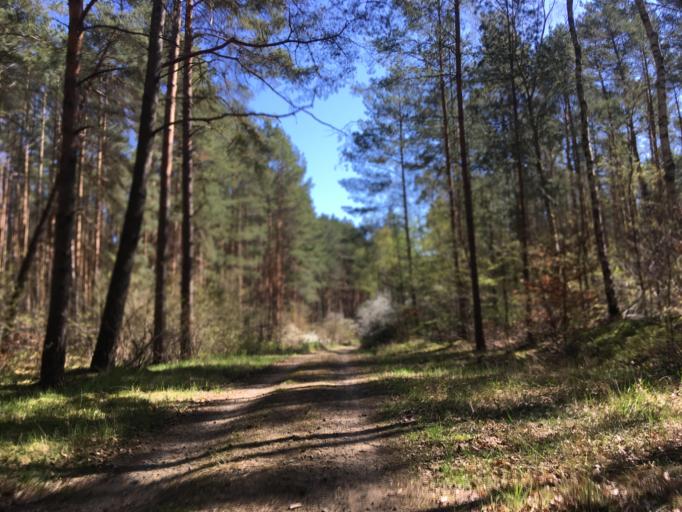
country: DE
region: Brandenburg
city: Bernau bei Berlin
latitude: 52.7037
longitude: 13.5219
